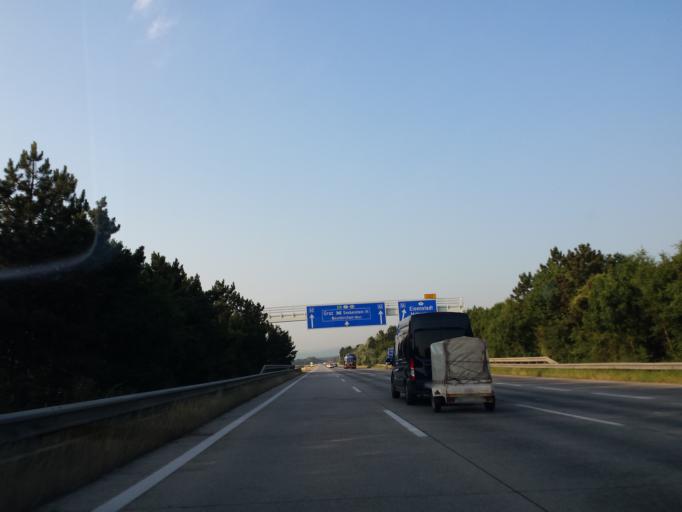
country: AT
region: Lower Austria
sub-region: Wiener Neustadt Stadt
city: Wiener Neustadt
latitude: 47.7843
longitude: 16.2046
